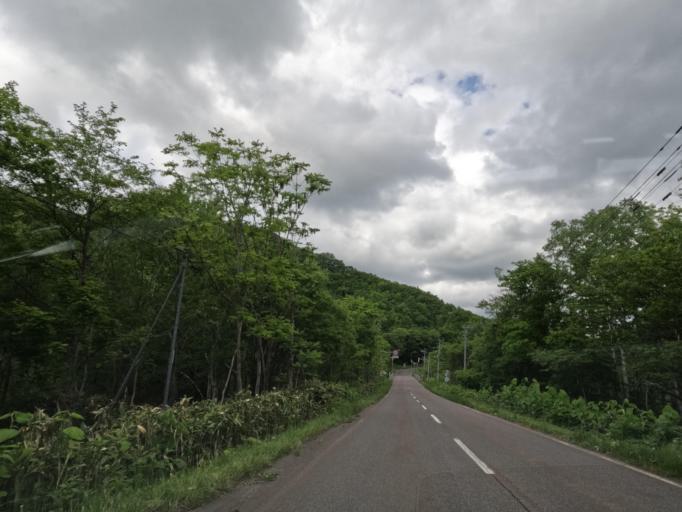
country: JP
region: Hokkaido
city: Takikawa
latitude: 43.5598
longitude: 141.6969
